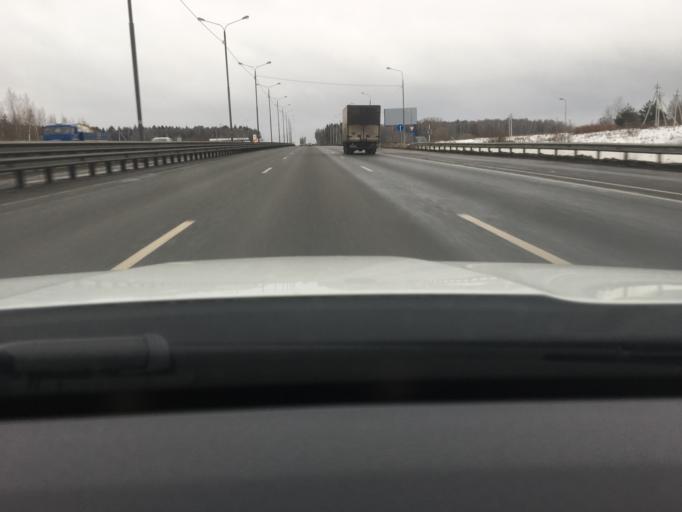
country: RU
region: Moskovskaya
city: Novyy Byt
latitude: 55.0735
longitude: 37.5718
